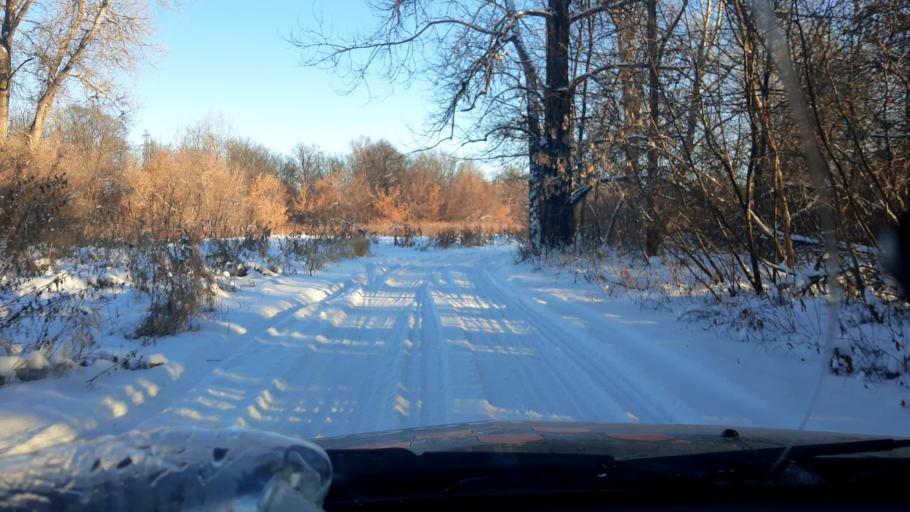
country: RU
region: Bashkortostan
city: Ufa
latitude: 54.6606
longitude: 55.9650
